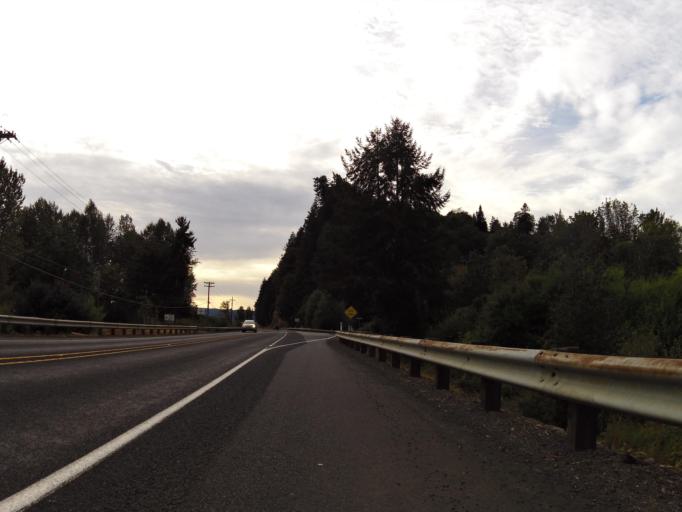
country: US
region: Oregon
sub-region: Columbia County
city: Clatskanie
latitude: 46.1900
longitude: -123.1227
